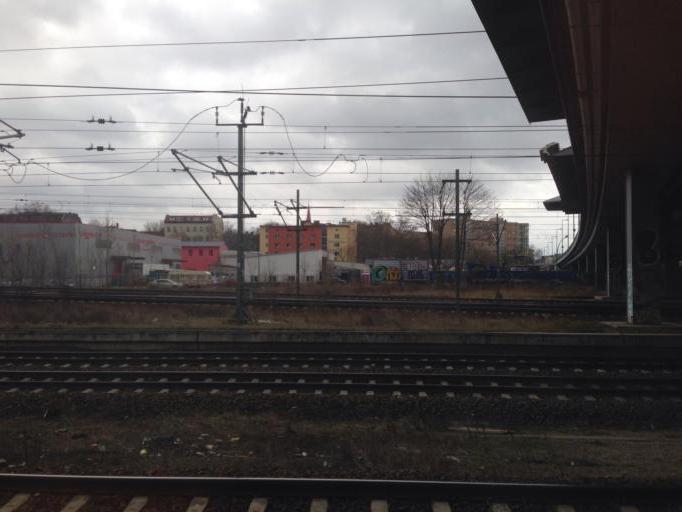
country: DE
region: Berlin
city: Moabit
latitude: 52.5360
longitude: 13.3438
